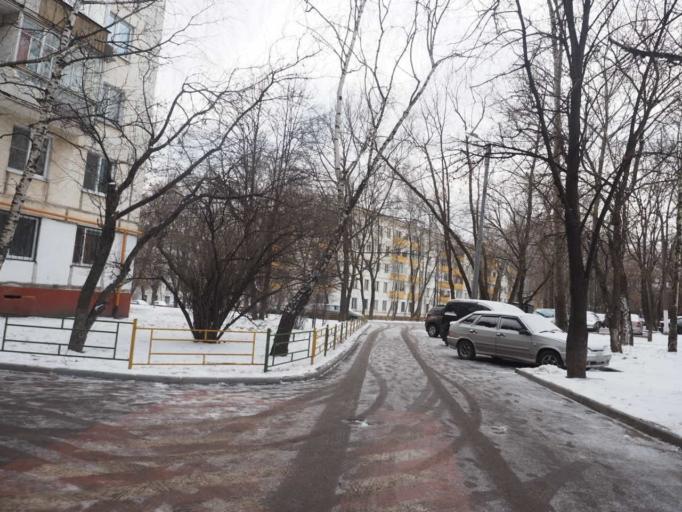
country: RU
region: Moscow
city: Orekhovo-Borisovo Severnoye
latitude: 55.6279
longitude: 37.6766
